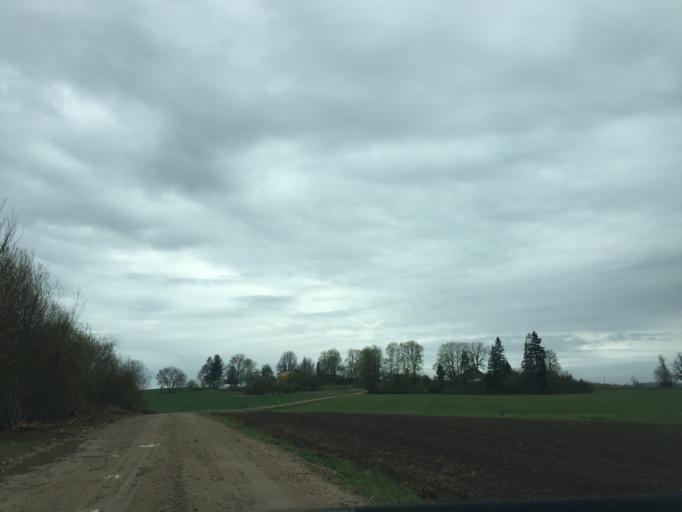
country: LV
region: Malpils
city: Malpils
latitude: 57.0245
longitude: 24.8470
